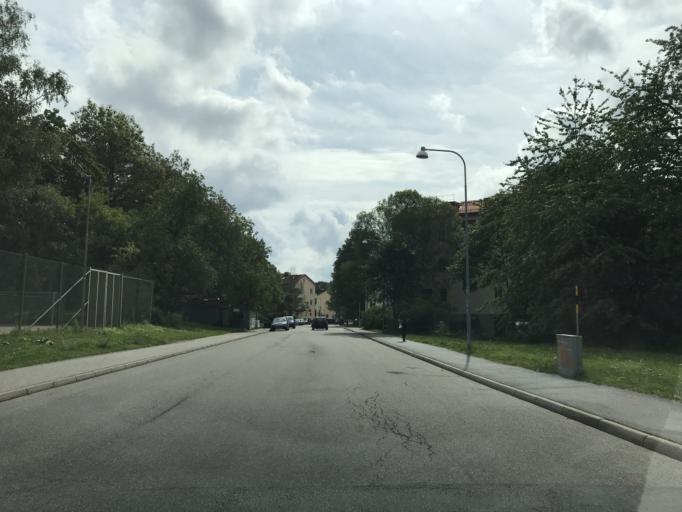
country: SE
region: Stockholm
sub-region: Sundbybergs Kommun
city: Sundbyberg
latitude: 59.3371
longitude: 17.9791
